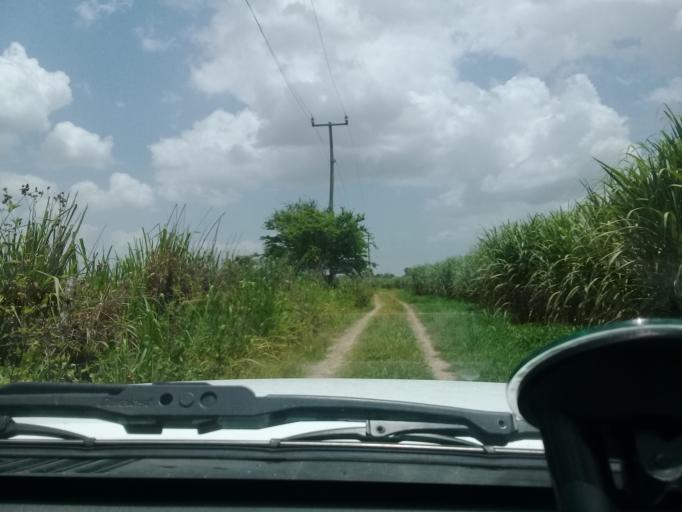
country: MX
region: Veracruz
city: Moralillo
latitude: 22.1338
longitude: -98.0384
